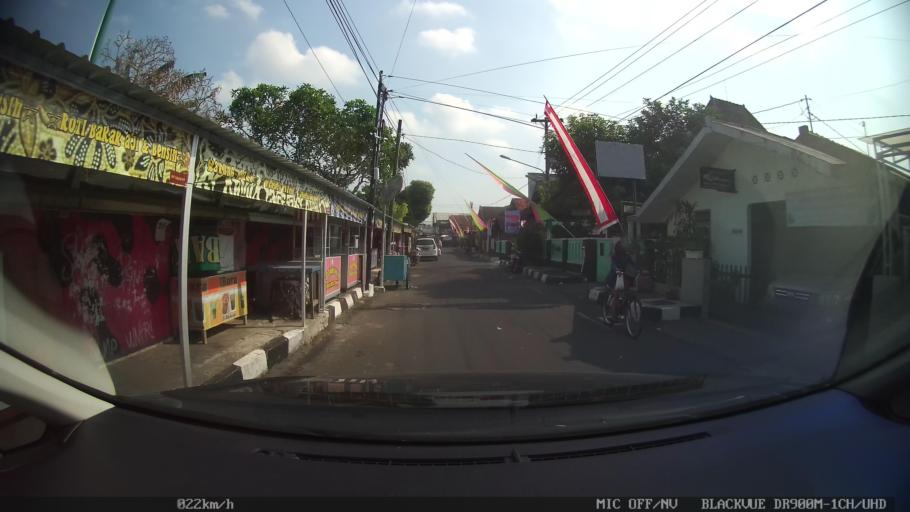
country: ID
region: Daerah Istimewa Yogyakarta
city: Yogyakarta
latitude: -7.8087
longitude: 110.3722
